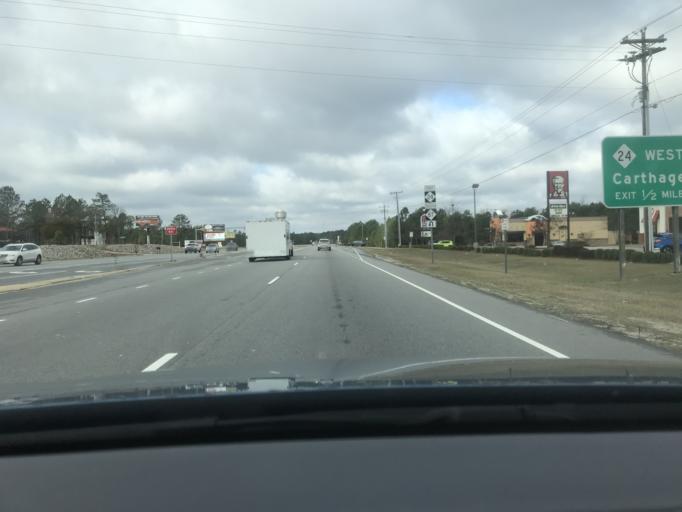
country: US
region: North Carolina
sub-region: Cumberland County
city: Spring Lake
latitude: 35.2614
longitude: -79.0469
